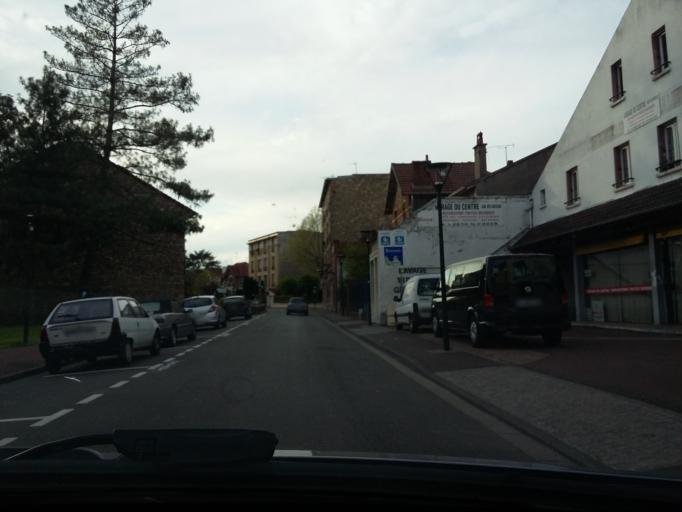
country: FR
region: Ile-de-France
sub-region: Departement du Val-d'Oise
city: Saint-Gratien
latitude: 48.9699
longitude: 2.2857
